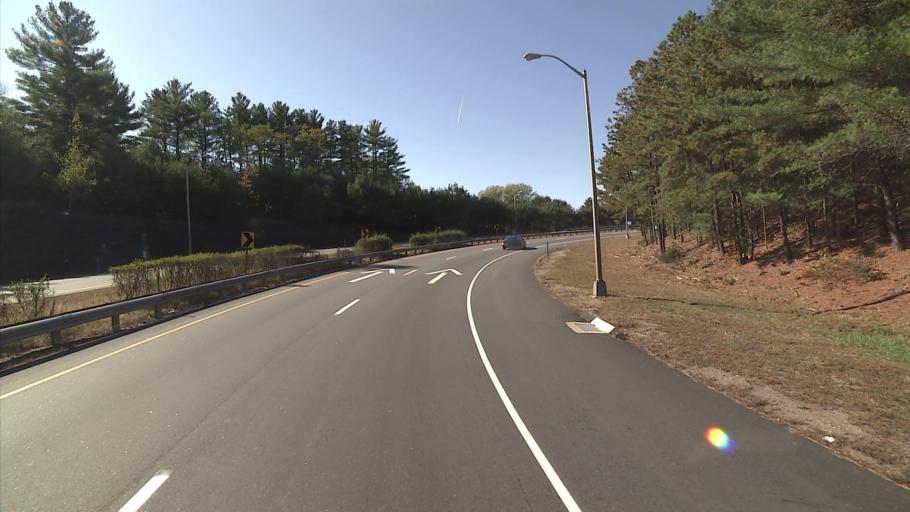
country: US
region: Connecticut
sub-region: Windham County
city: Willimantic
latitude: 41.7336
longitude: -72.1816
